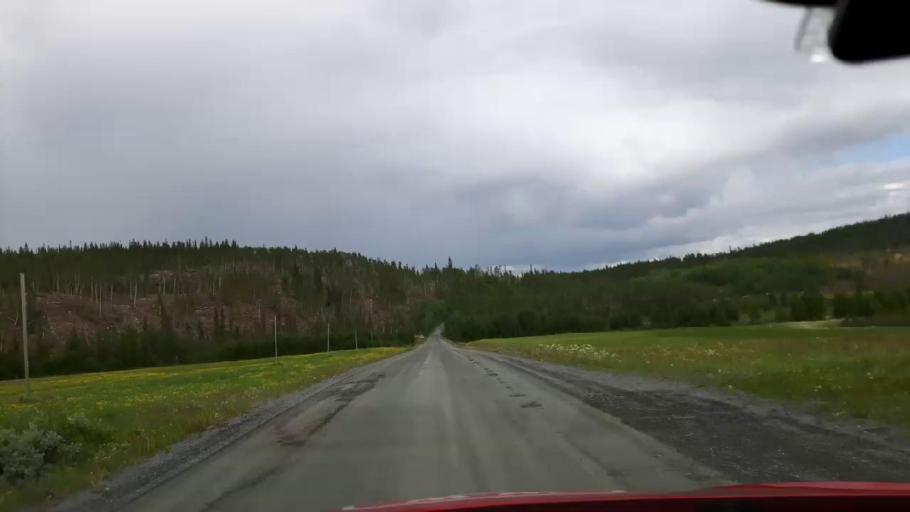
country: NO
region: Nord-Trondelag
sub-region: Lierne
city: Sandvika
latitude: 64.1481
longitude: 13.9579
